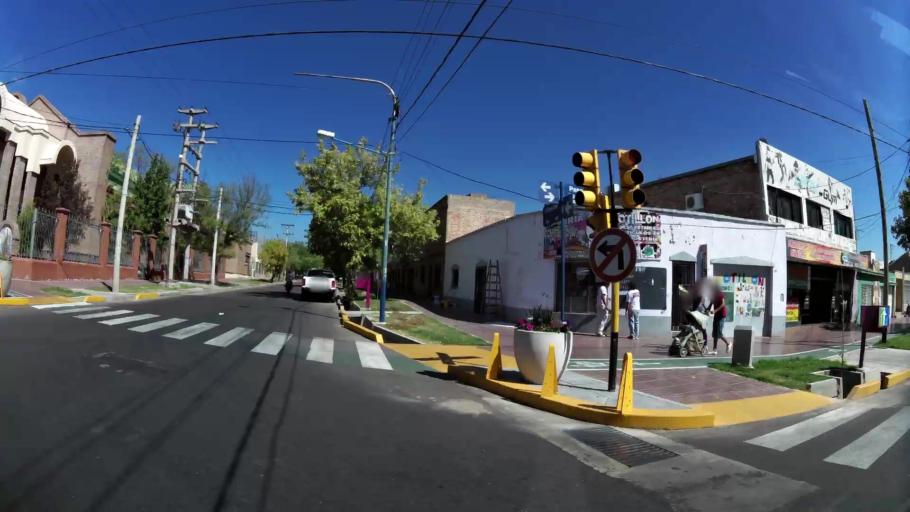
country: AR
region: Mendoza
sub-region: Departamento de Godoy Cruz
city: Godoy Cruz
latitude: -32.9056
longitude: -68.8603
